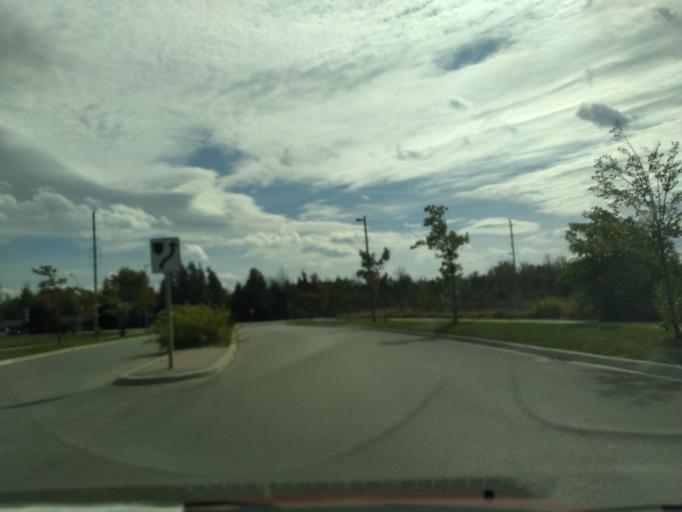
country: CA
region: Ontario
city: Keswick
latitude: 44.3012
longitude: -79.3766
